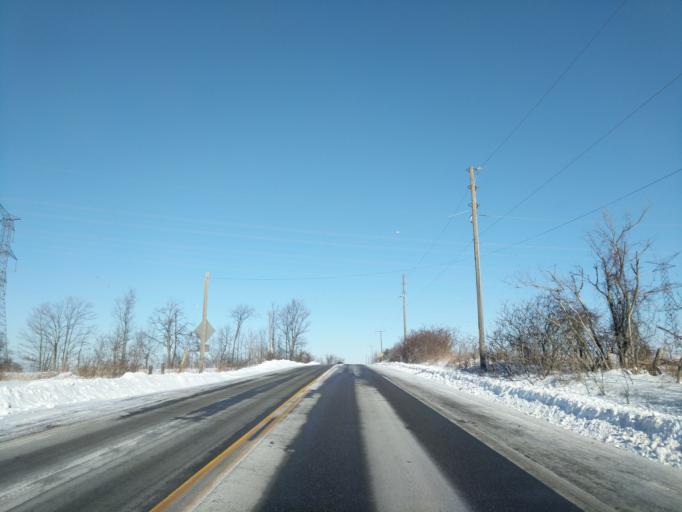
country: CA
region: Ontario
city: Pickering
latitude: 43.8509
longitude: -79.1297
